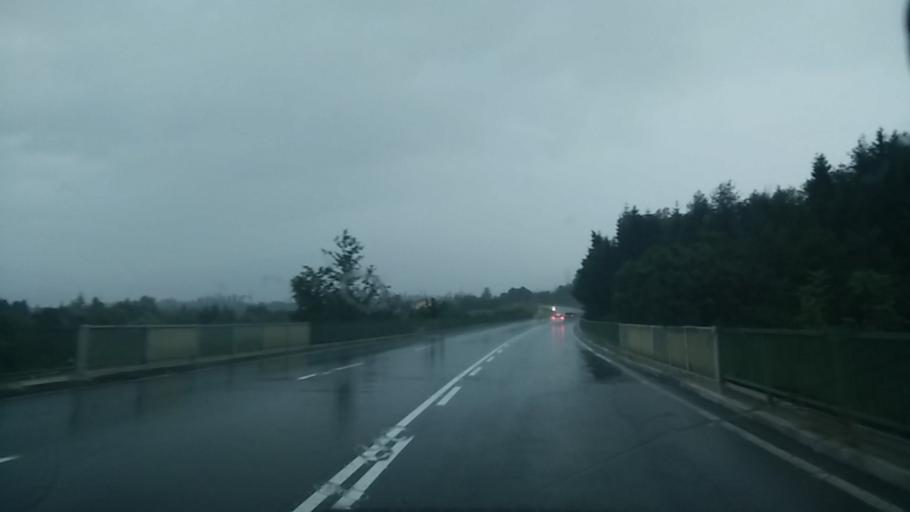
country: AT
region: Carinthia
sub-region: Politischer Bezirk Villach Land
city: Wernberg
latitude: 46.6244
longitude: 13.9190
